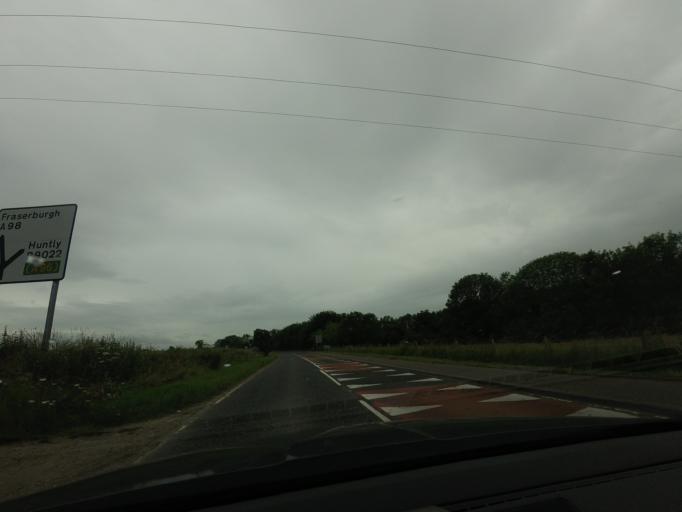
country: GB
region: Scotland
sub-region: Aberdeenshire
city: Portsoy
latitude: 57.6757
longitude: -2.6880
